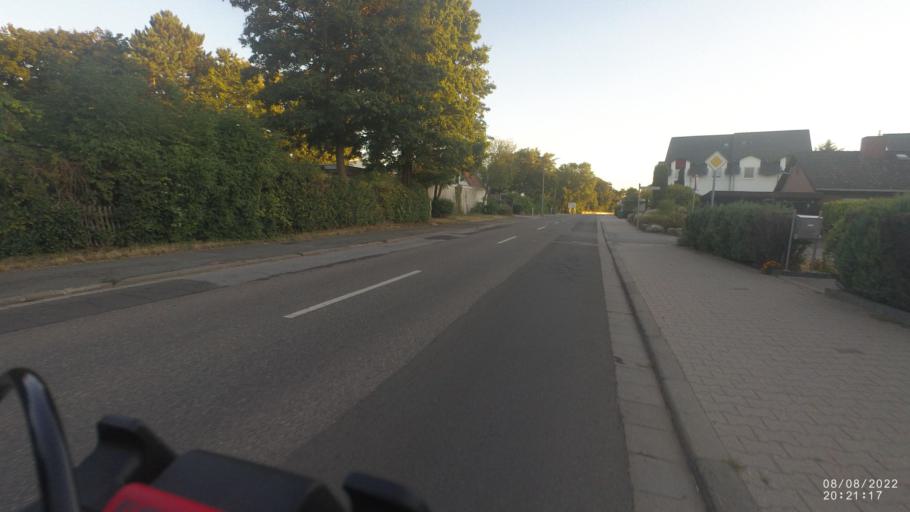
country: DE
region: Rheinland-Pfalz
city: Worrstadt
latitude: 49.8489
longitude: 8.1206
